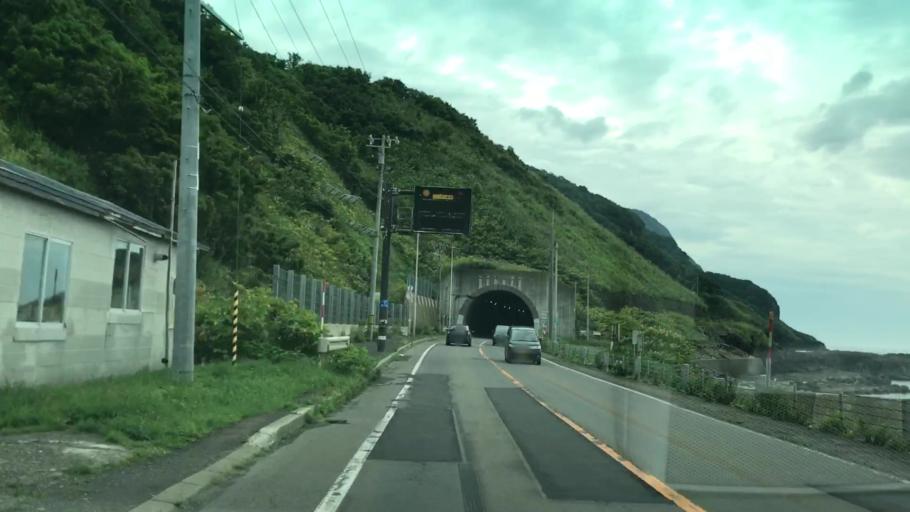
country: JP
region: Hokkaido
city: Iwanai
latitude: 42.9618
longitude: 140.4630
